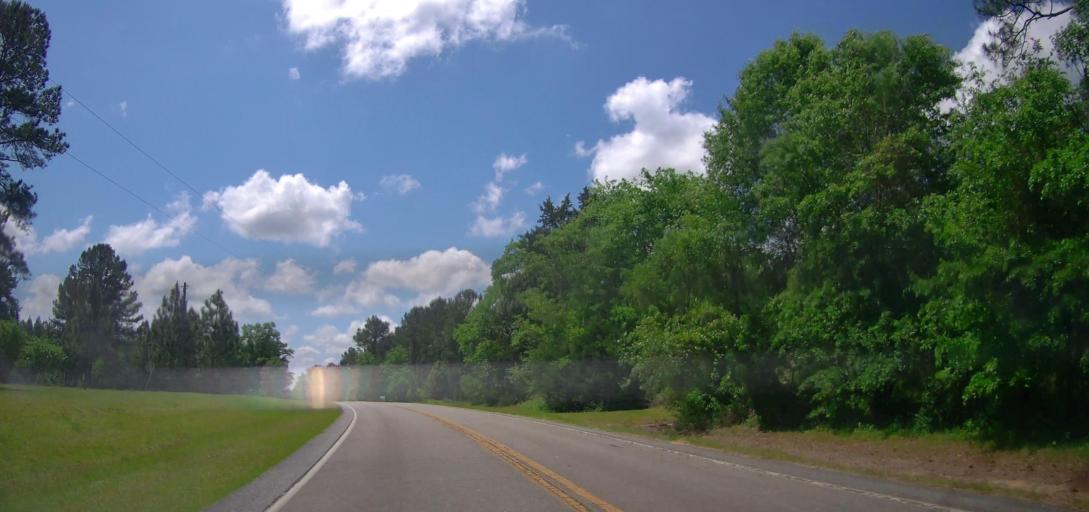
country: US
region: Georgia
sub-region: Bleckley County
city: Cochran
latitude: 32.4583
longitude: -83.2861
